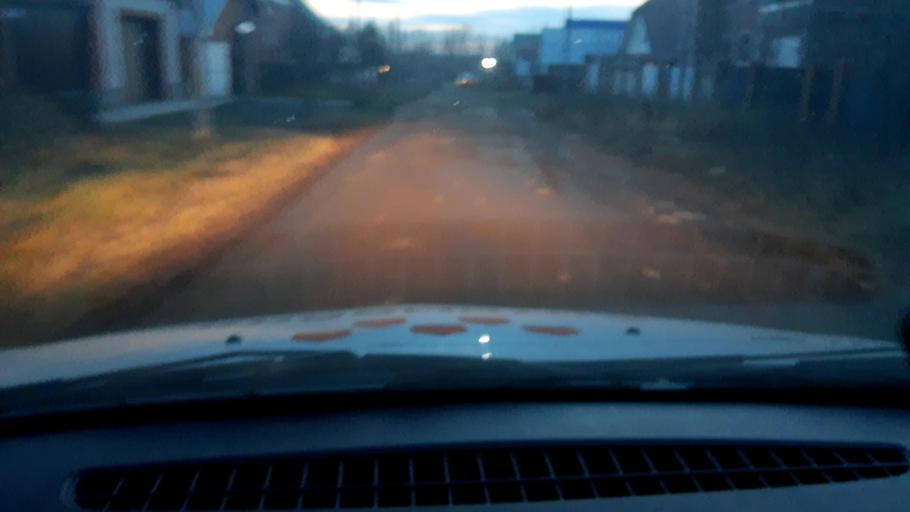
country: RU
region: Bashkortostan
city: Iglino
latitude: 54.7789
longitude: 56.2359
